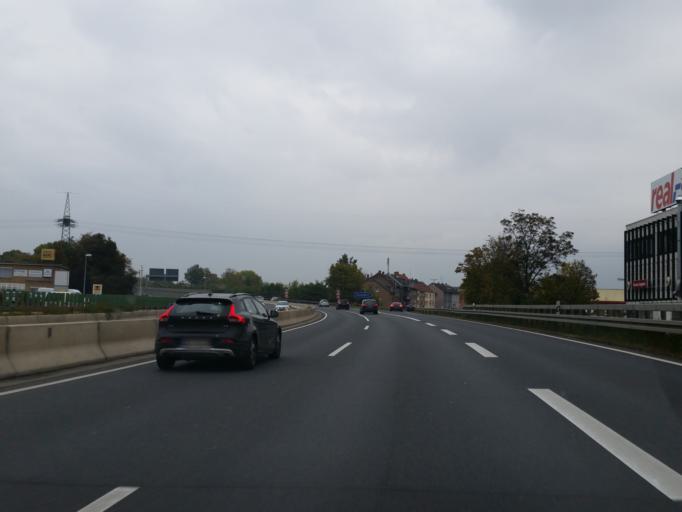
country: DE
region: Lower Saxony
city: Braunschweig
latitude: 52.2423
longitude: 10.5099
